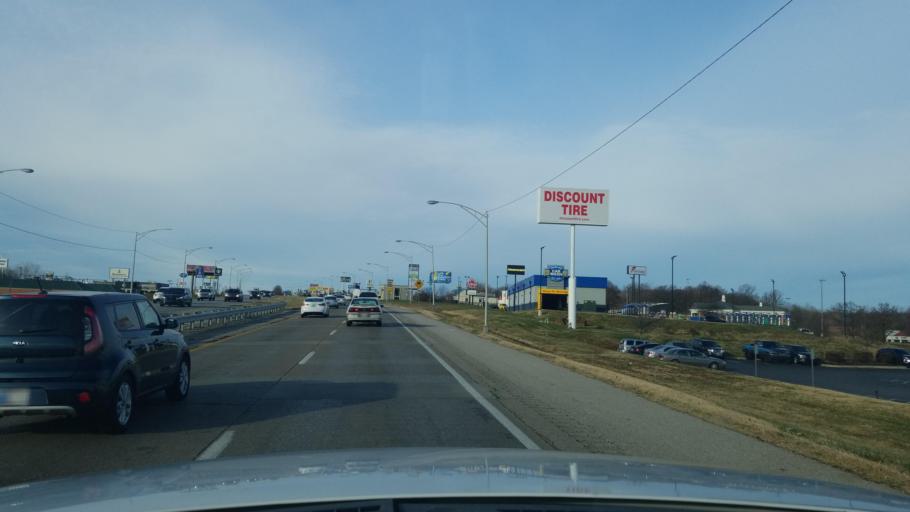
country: US
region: Indiana
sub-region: Vanderburgh County
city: Evansville
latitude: 37.9778
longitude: -87.6292
